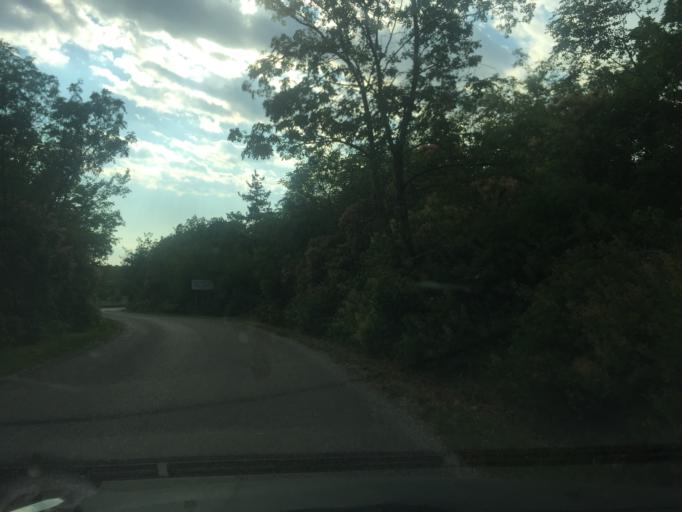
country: IT
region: Friuli Venezia Giulia
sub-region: Provincia di Gorizia
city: Doberdo del Lago
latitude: 45.8756
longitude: 13.5405
